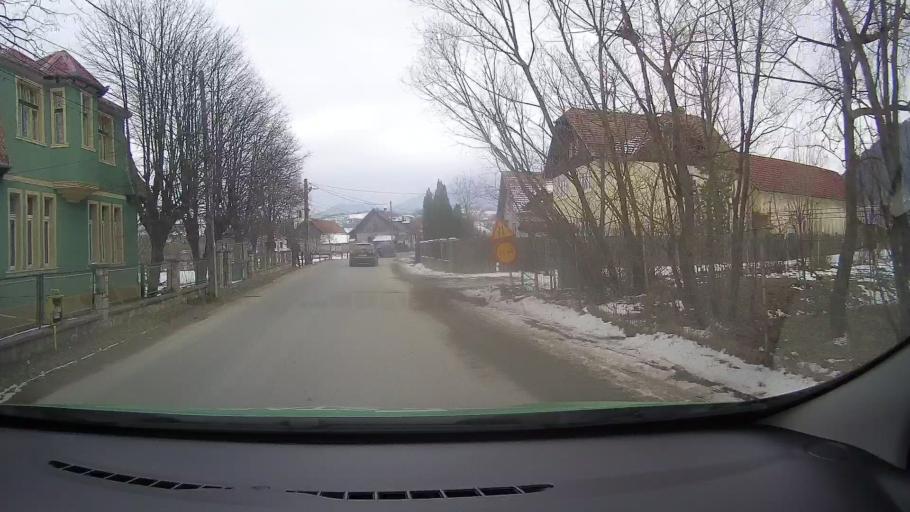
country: RO
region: Brasov
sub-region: Comuna Bran
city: Bran
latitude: 45.5281
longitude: 25.3606
